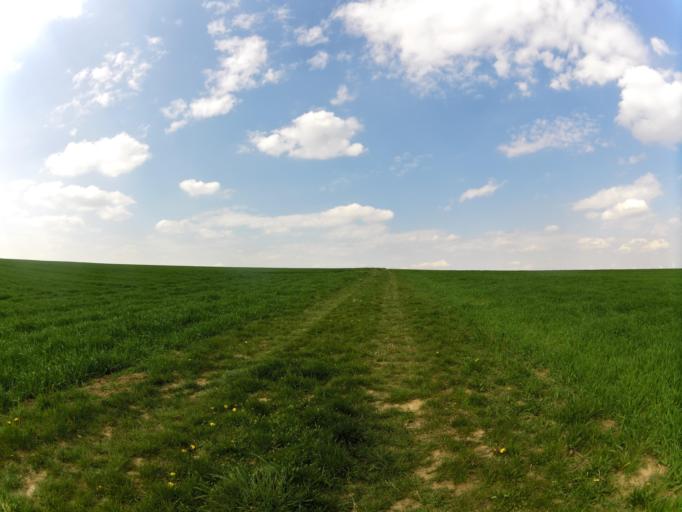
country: DE
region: Bavaria
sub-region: Regierungsbezirk Unterfranken
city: Winterhausen
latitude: 49.6888
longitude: 10.0084
